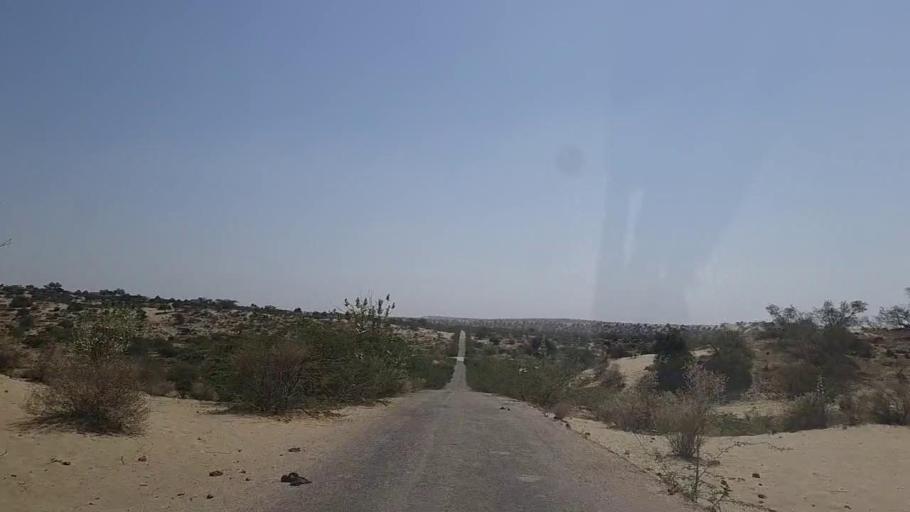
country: PK
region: Sindh
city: Diplo
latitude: 24.4996
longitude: 69.4292
